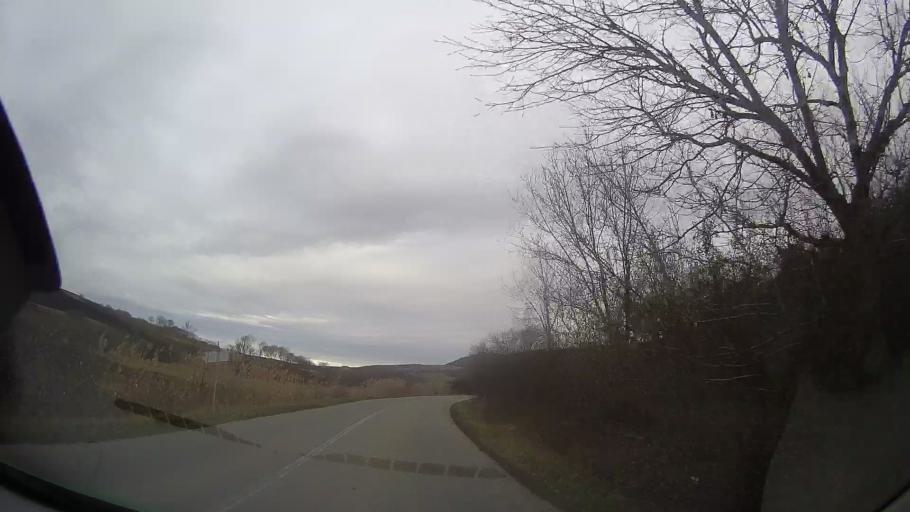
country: RO
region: Mures
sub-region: Comuna Bala
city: Bala
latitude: 46.7279
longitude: 24.5429
